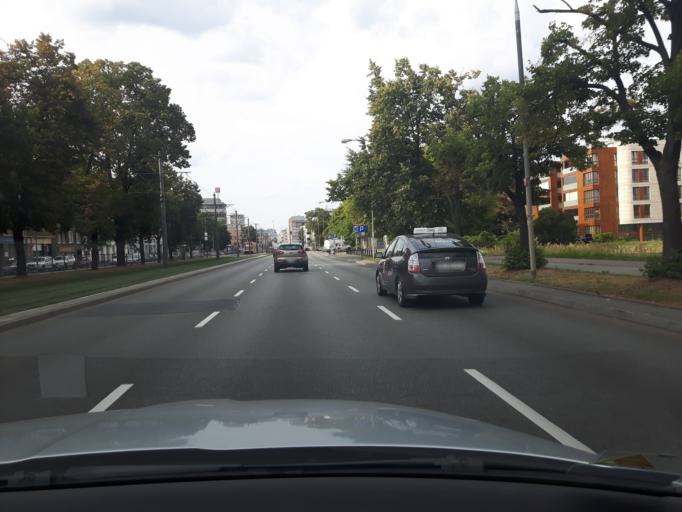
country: PL
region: Masovian Voivodeship
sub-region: Warszawa
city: Mokotow
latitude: 52.1955
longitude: 21.0244
